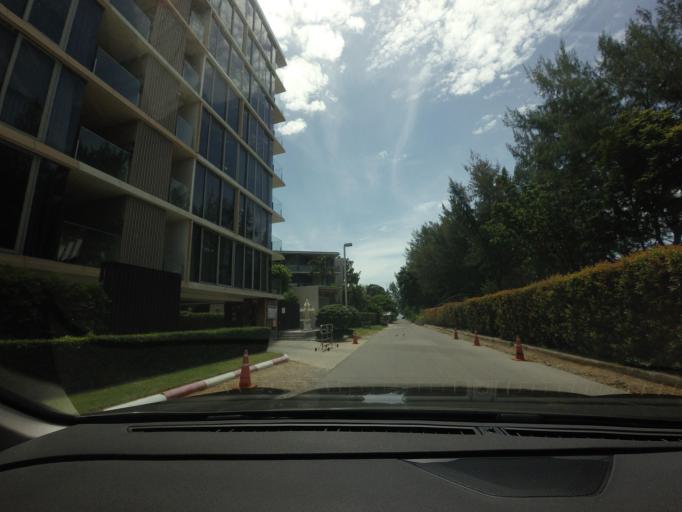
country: TH
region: Prachuap Khiri Khan
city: Hua Hin
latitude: 12.5106
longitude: 99.9757
